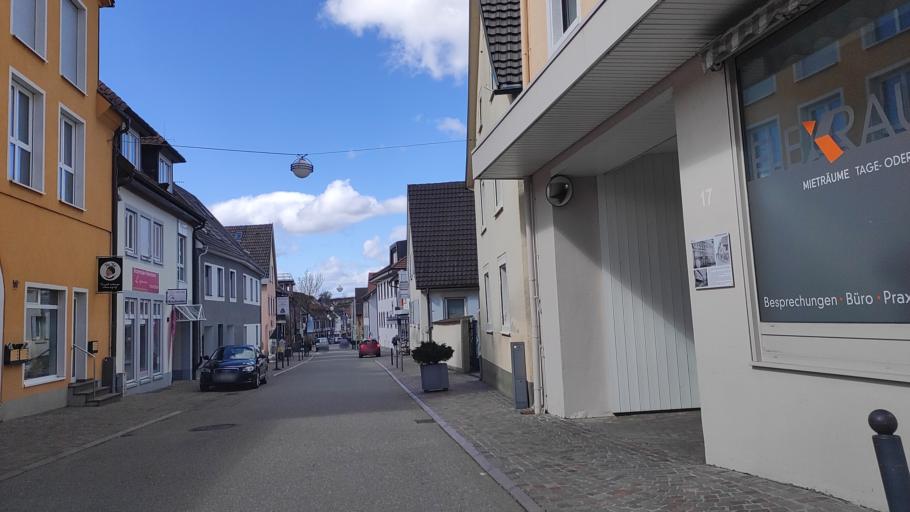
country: DE
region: Baden-Wuerttemberg
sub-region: Freiburg Region
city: Heitersheim
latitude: 47.8719
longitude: 7.6632
